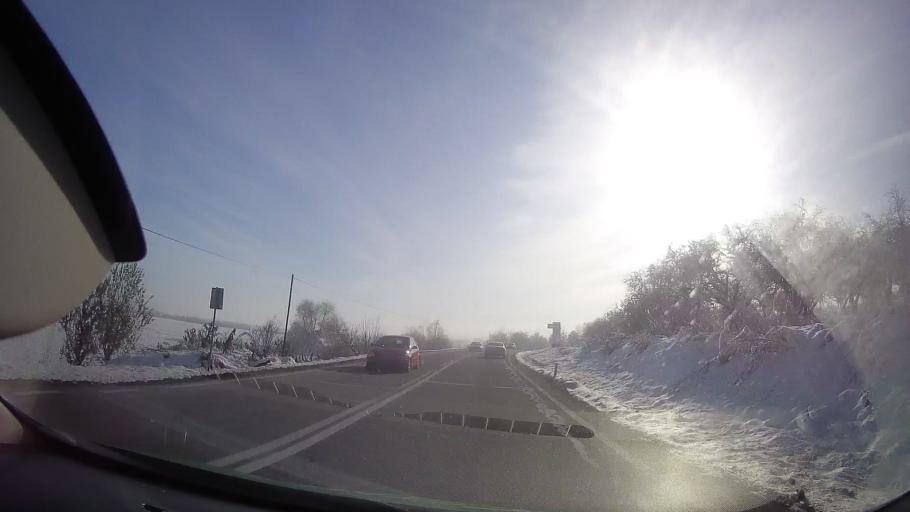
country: RO
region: Neamt
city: Bodesti
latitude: 47.0091
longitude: 26.4245
